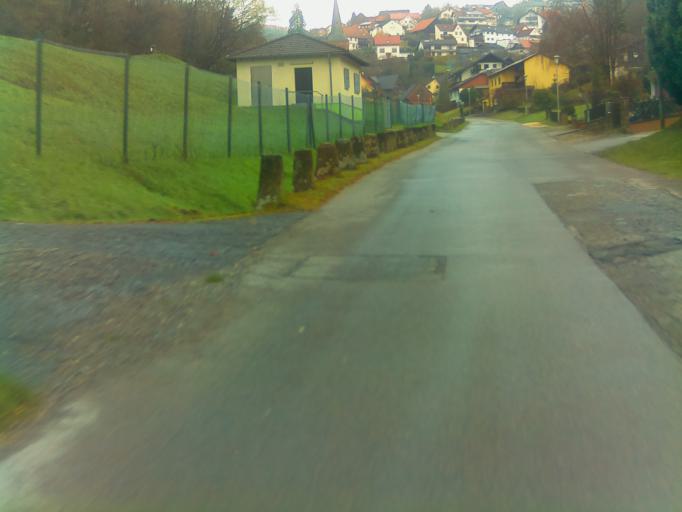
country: DE
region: Baden-Wuerttemberg
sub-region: Karlsruhe Region
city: Heddesbach
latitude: 49.4846
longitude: 8.8687
